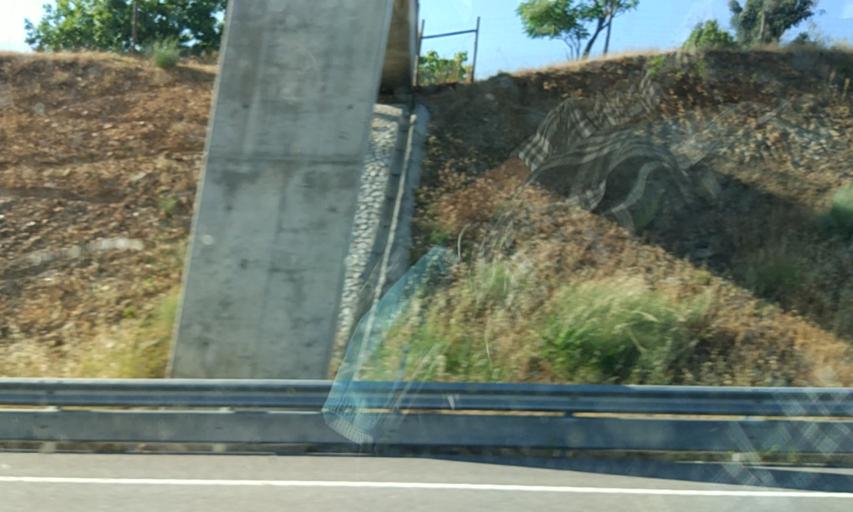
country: PT
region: Vila Real
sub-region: Murca
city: Murca
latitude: 41.4326
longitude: -7.3417
